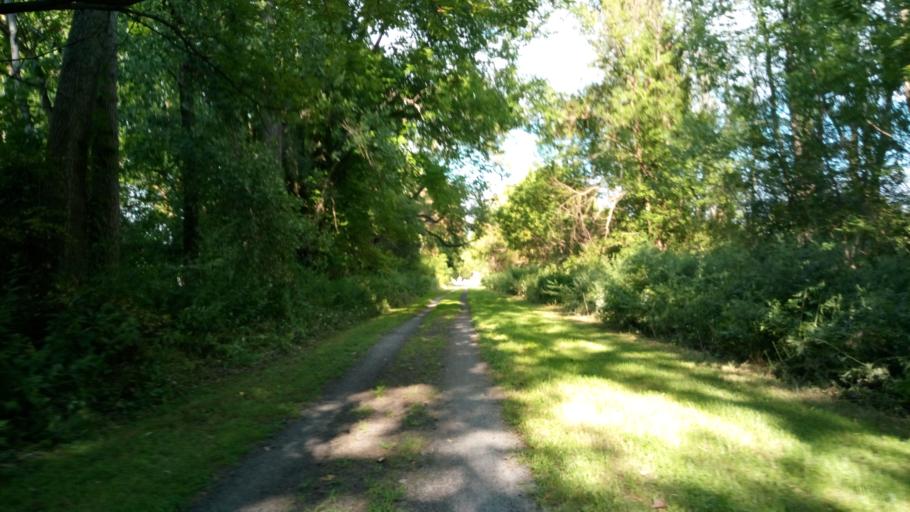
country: US
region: New York
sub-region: Monroe County
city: Honeoye Falls
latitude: 42.9920
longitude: -77.5278
